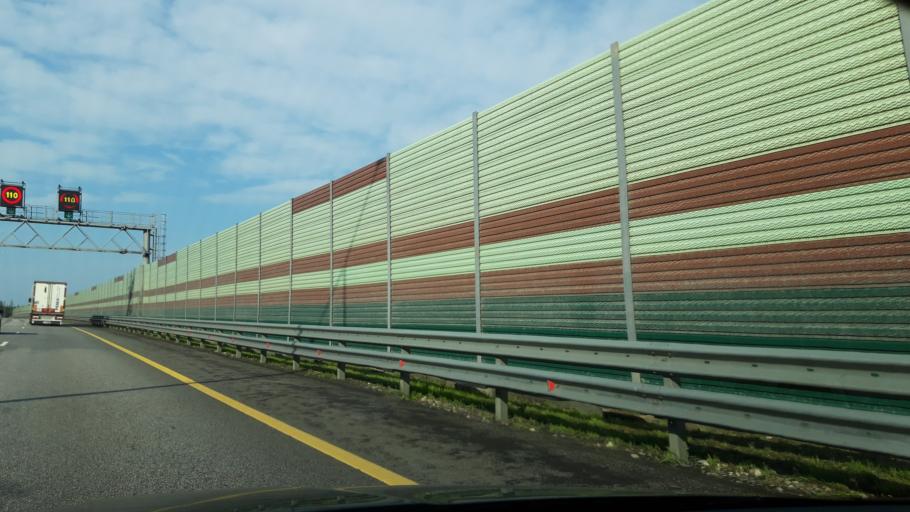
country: RU
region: Moskovskaya
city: Solnechnogorsk
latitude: 56.1451
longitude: 37.0090
